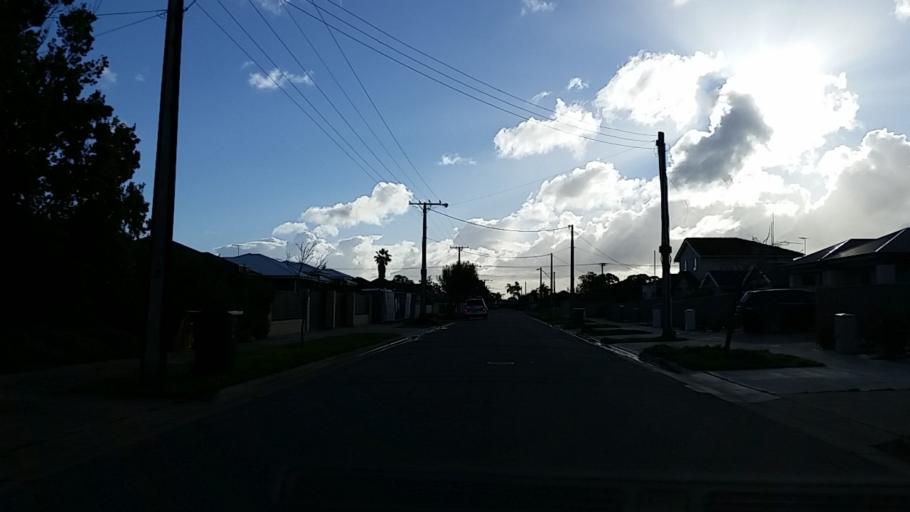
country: AU
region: South Australia
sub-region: Charles Sturt
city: Woodville West
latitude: -34.8879
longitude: 138.5211
